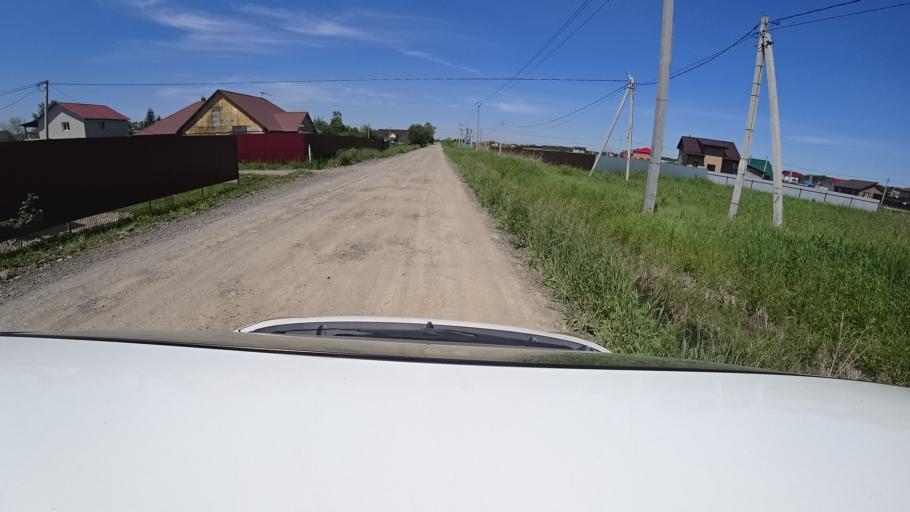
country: RU
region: Khabarovsk Krai
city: Topolevo
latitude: 48.5109
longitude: 135.1957
